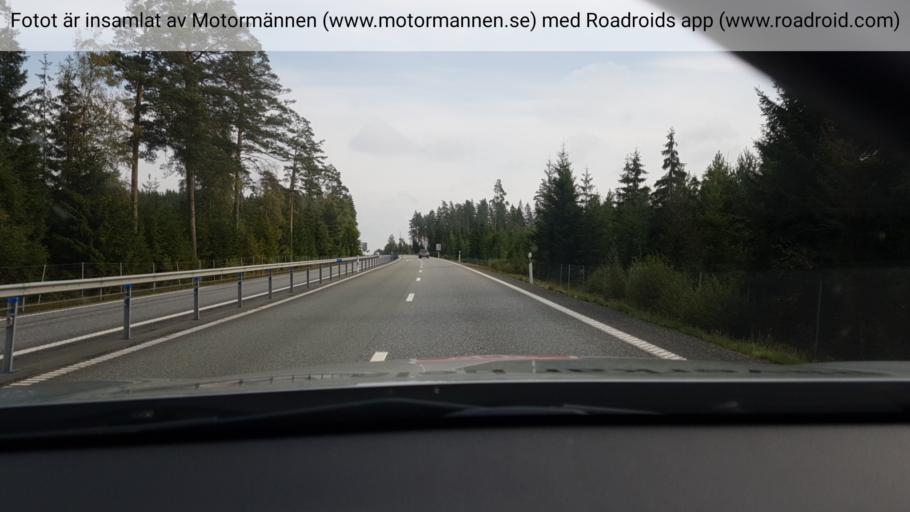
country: SE
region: Joenkoeping
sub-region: Mullsjo Kommun
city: Mullsjoe
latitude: 57.7557
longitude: 13.8588
